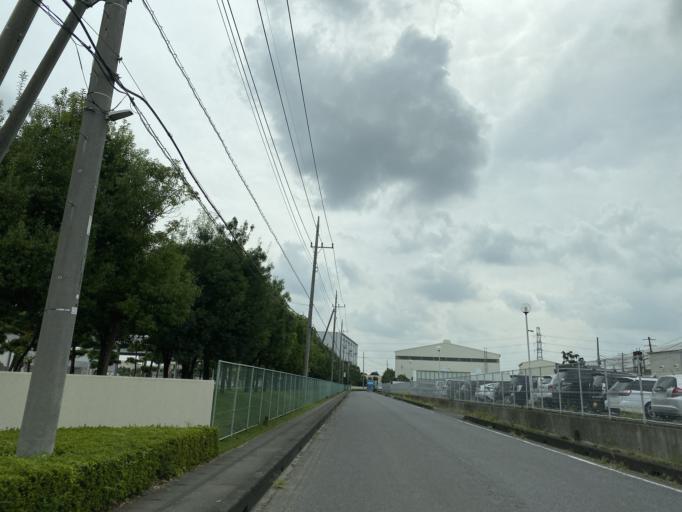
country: JP
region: Ibaraki
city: Mitsukaido
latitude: 36.0234
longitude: 140.0494
